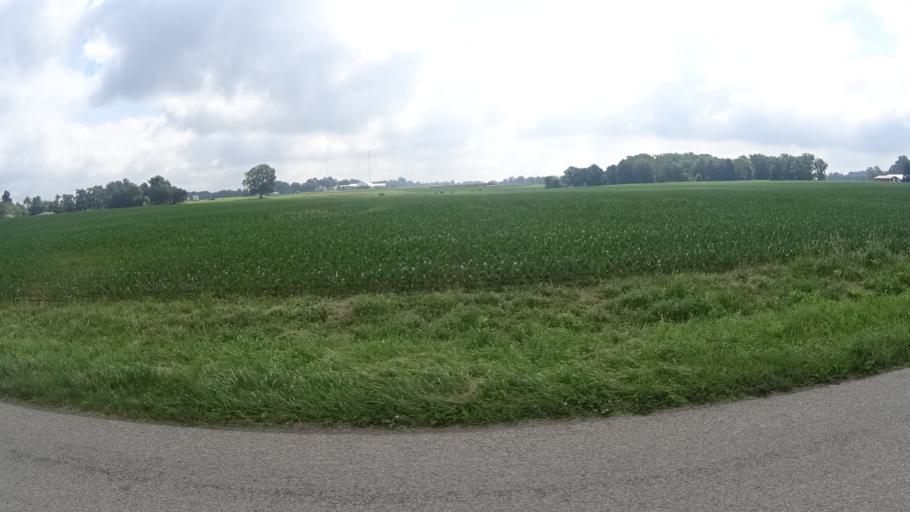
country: US
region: Ohio
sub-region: Huron County
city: Wakeman
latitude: 41.3046
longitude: -82.4659
